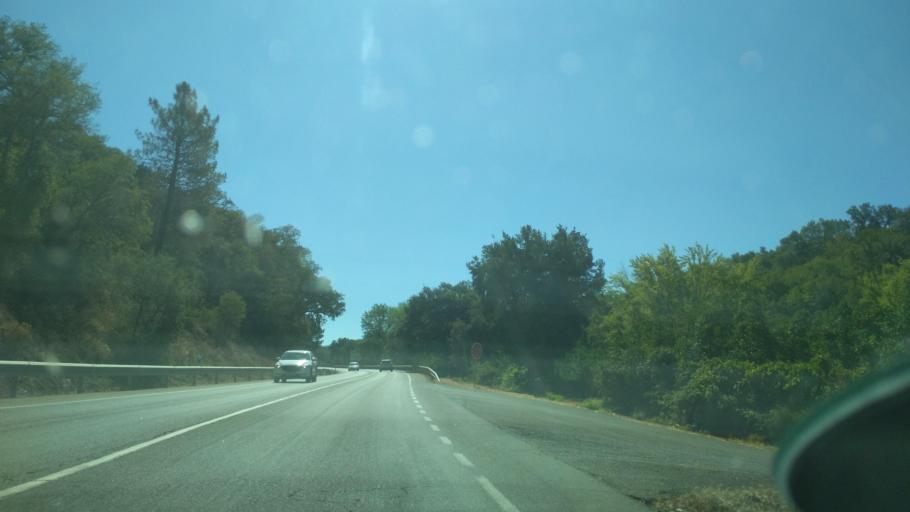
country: ES
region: Andalusia
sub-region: Provincia de Huelva
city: Fuenteheridos
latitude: 37.9170
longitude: -6.6713
